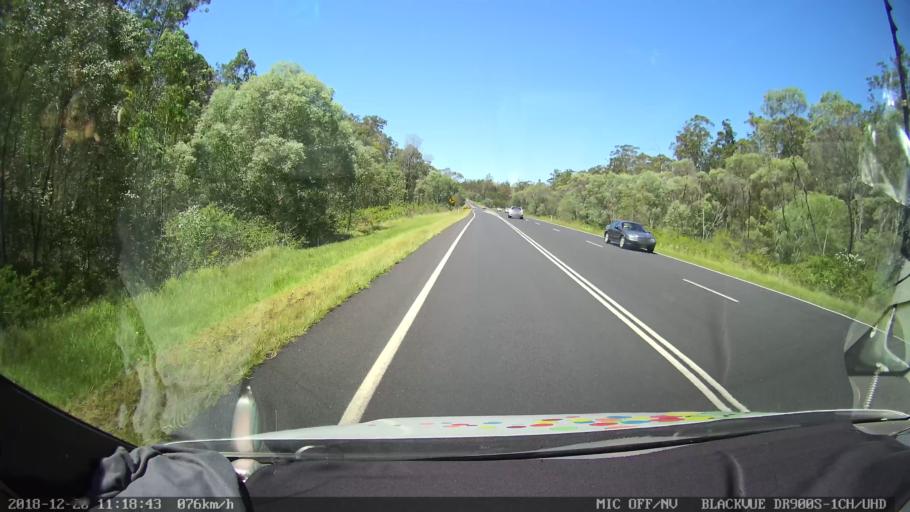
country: AU
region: New South Wales
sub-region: Richmond Valley
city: Casino
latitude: -29.0547
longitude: 153.0060
